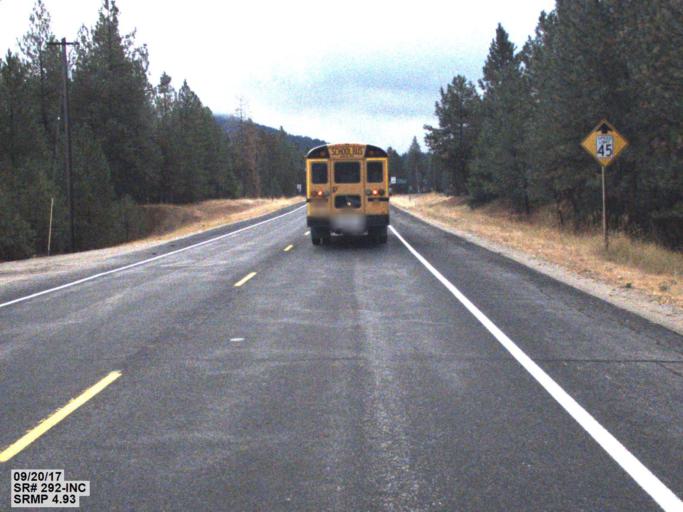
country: US
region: Washington
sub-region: Spokane County
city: Deer Park
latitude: 48.0637
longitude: -117.6399
